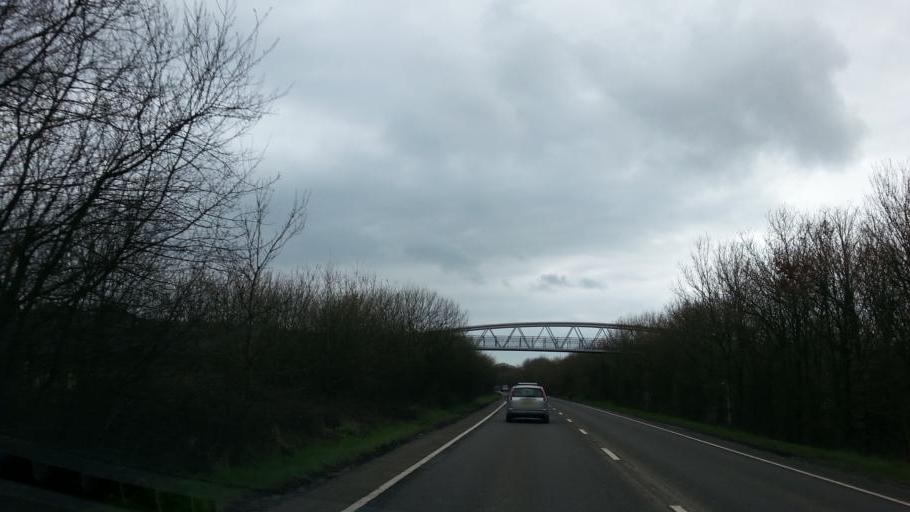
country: GB
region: England
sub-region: Devon
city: Fremington
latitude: 51.0627
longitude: -4.0884
